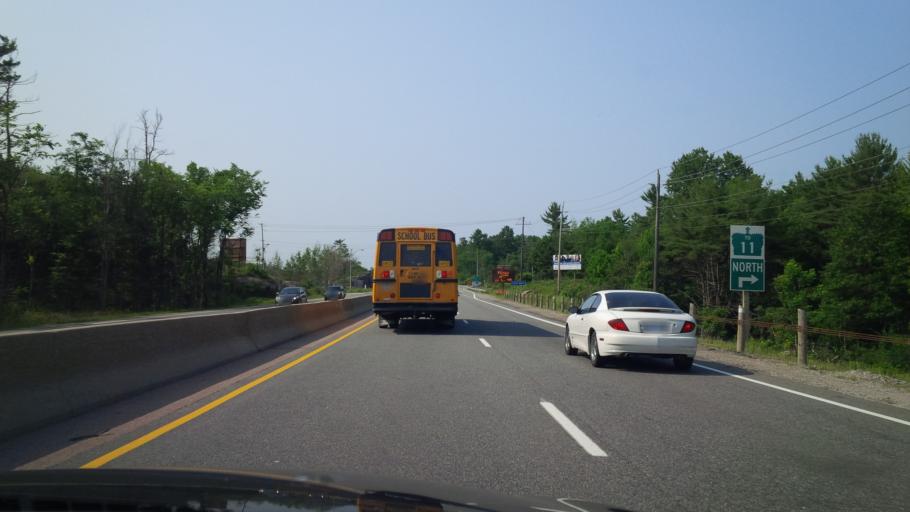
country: CA
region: Ontario
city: Gravenhurst
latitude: 44.7831
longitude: -79.3341
